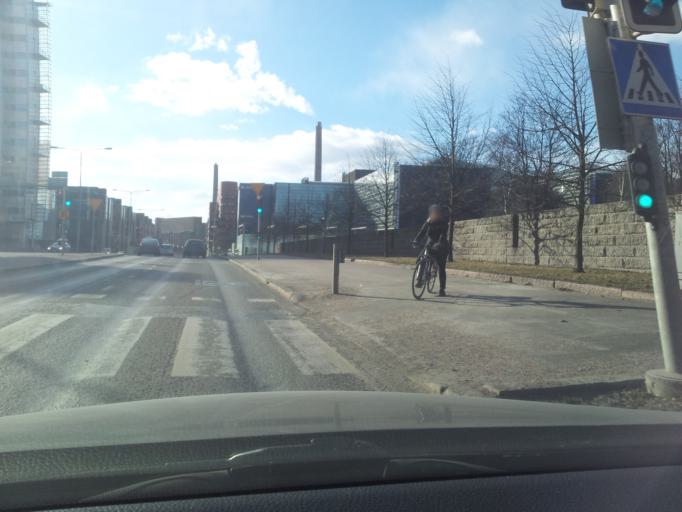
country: FI
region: Uusimaa
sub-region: Helsinki
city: Helsinki
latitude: 60.1646
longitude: 24.9169
